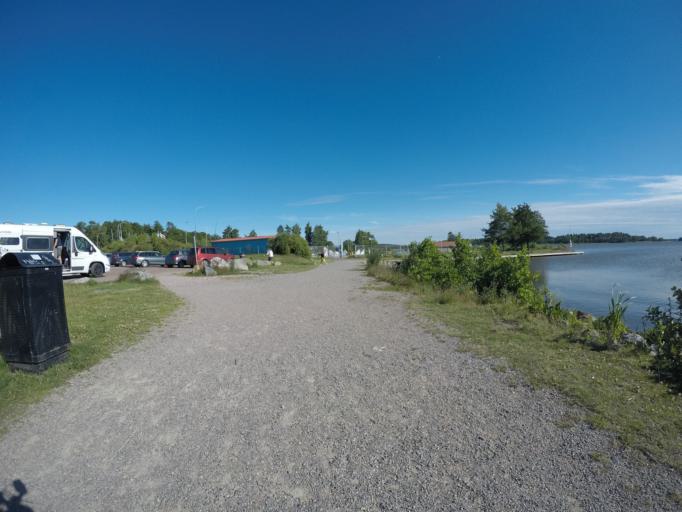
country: SE
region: Vaestmanland
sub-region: Vasteras
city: Vasteras
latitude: 59.5960
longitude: 16.5873
